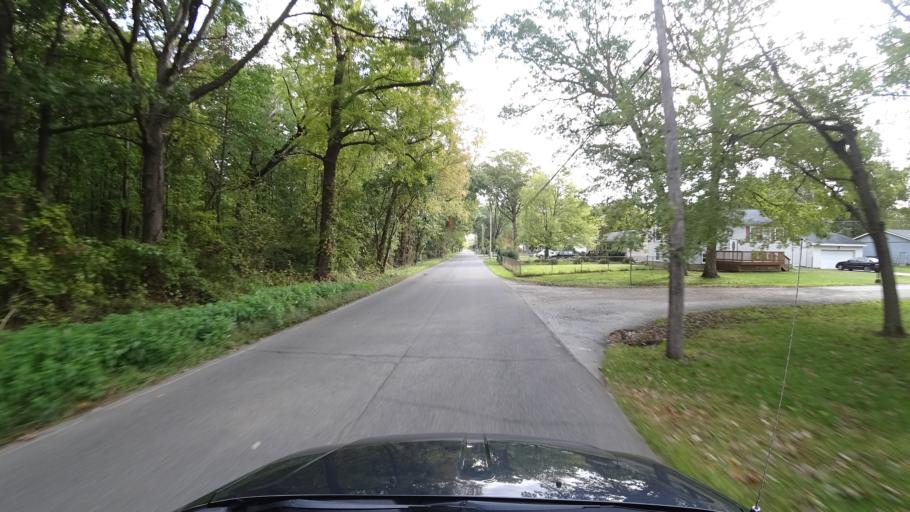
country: US
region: Indiana
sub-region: LaPorte County
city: Trail Creek
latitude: 41.6911
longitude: -86.8670
